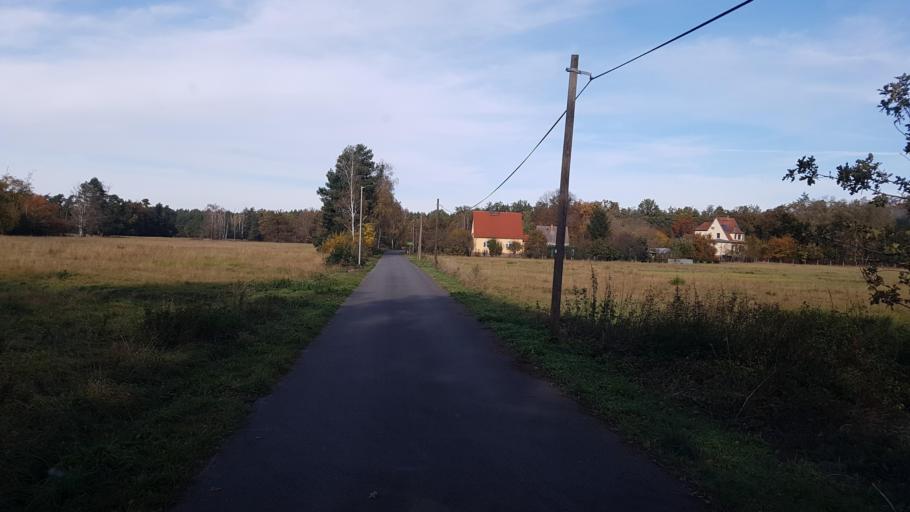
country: DE
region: Brandenburg
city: Tettau
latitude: 51.4292
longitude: 13.7578
